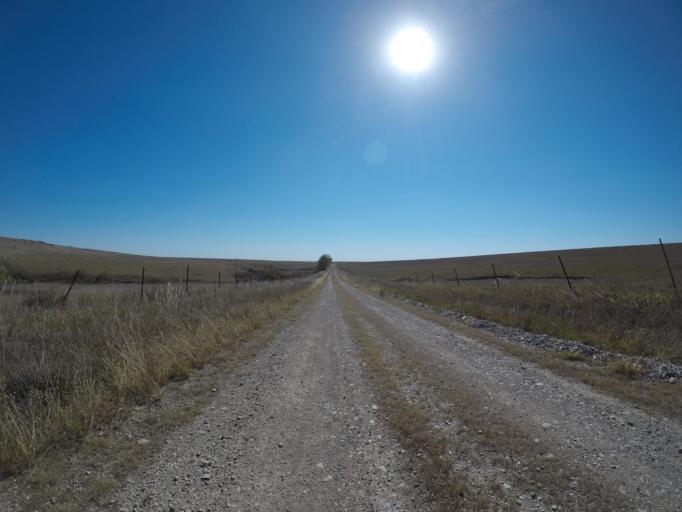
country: US
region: Kansas
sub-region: Wabaunsee County
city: Alma
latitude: 39.0285
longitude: -96.4094
